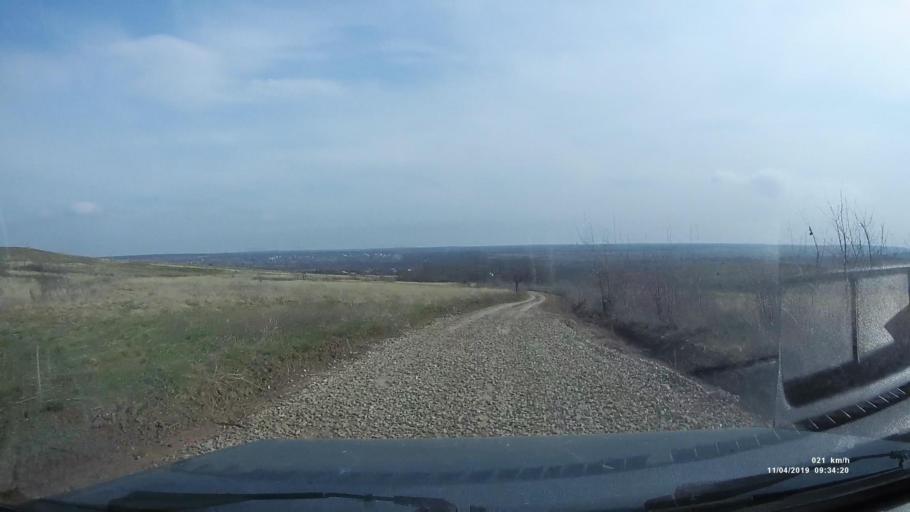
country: RU
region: Rostov
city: Staraya Stanitsa
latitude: 48.2687
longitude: 40.3693
